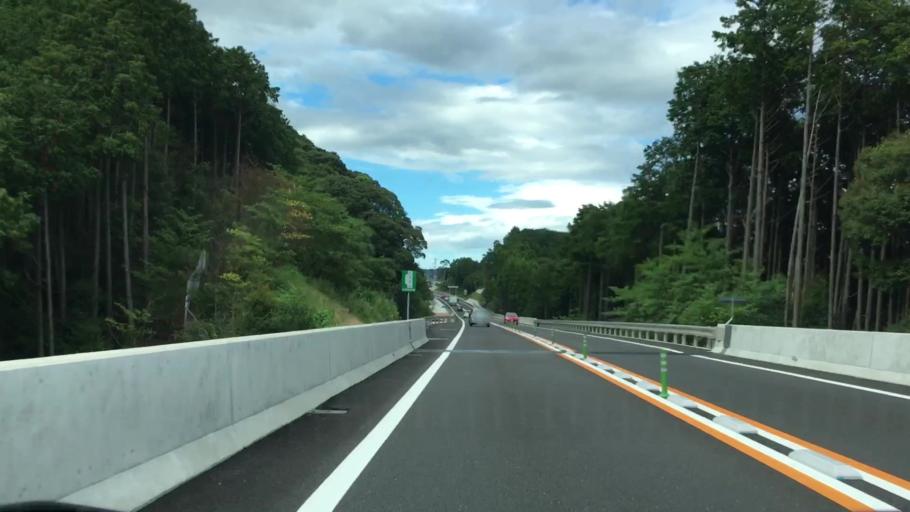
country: JP
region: Saga Prefecture
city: Imaricho-ko
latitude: 33.3259
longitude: 129.9273
